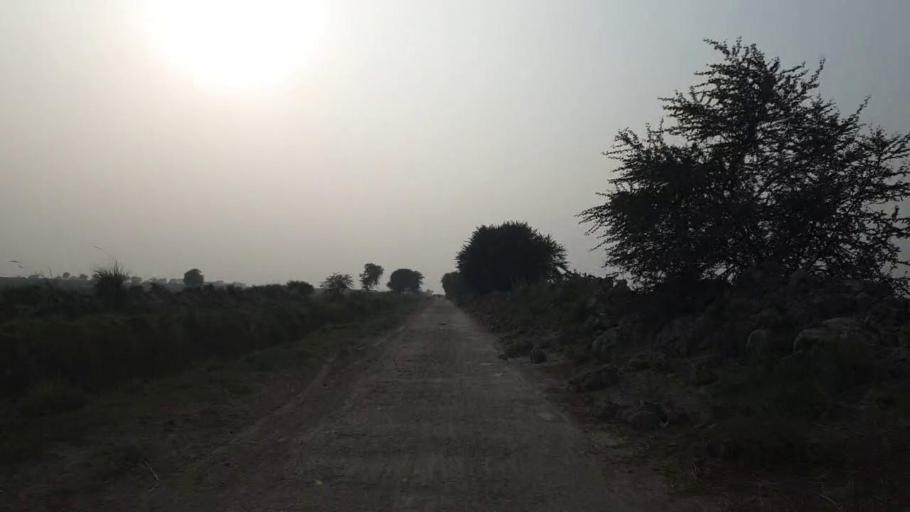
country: PK
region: Sindh
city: Mirpur Batoro
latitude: 24.6545
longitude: 68.3840
